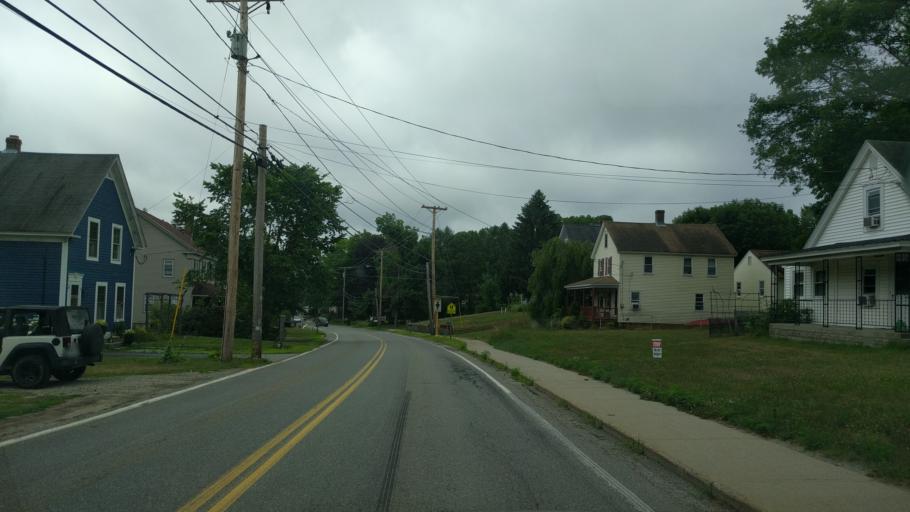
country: US
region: Massachusetts
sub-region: Worcester County
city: Grafton
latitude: 42.2387
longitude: -71.7050
